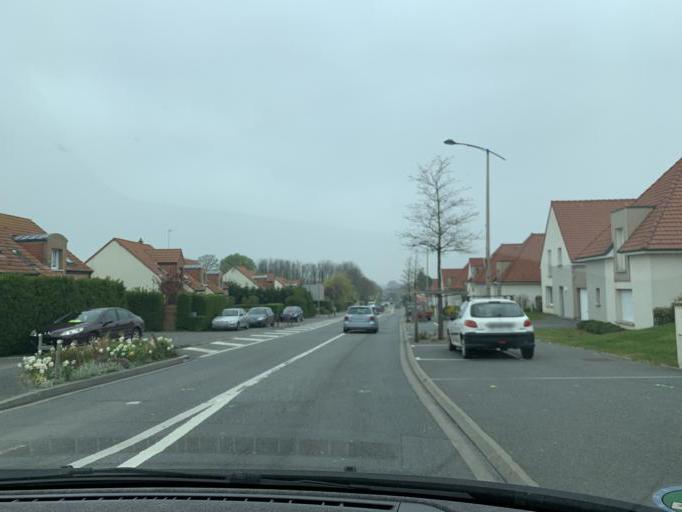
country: FR
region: Nord-Pas-de-Calais
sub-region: Departement du Pas-de-Calais
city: Coquelles
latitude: 50.9299
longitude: 1.7983
